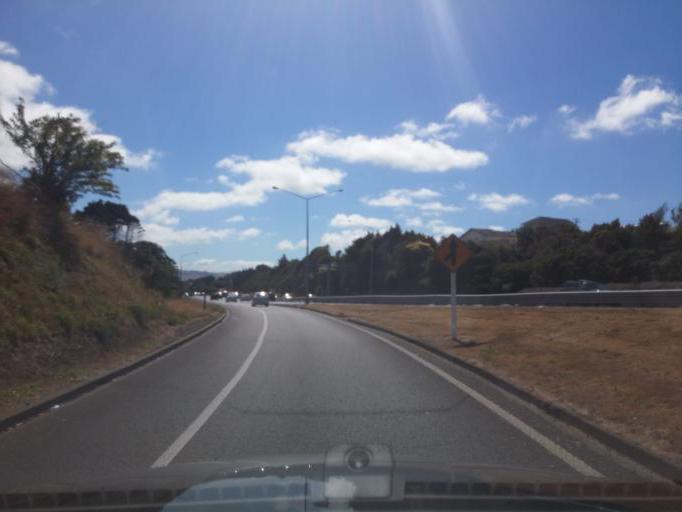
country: NZ
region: Wellington
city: Petone
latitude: -41.2203
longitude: 174.8094
